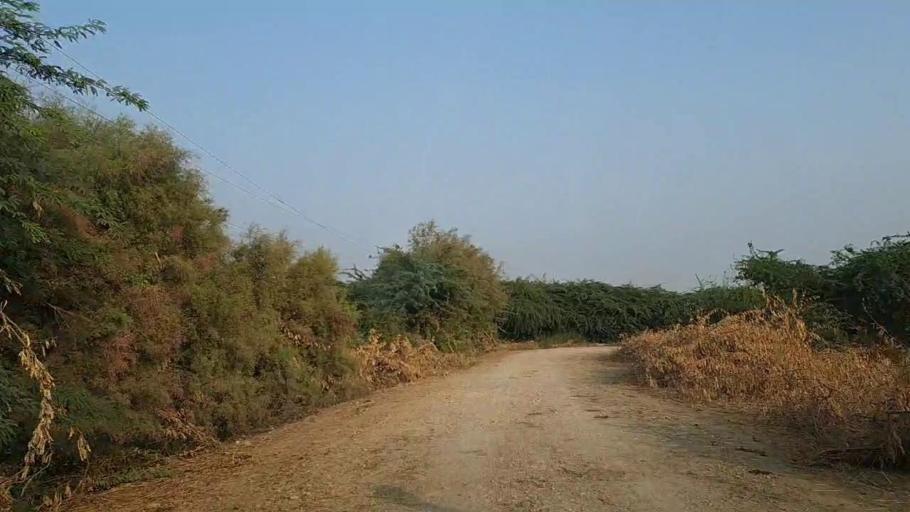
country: PK
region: Sindh
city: Thatta
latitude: 24.6920
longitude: 67.8086
